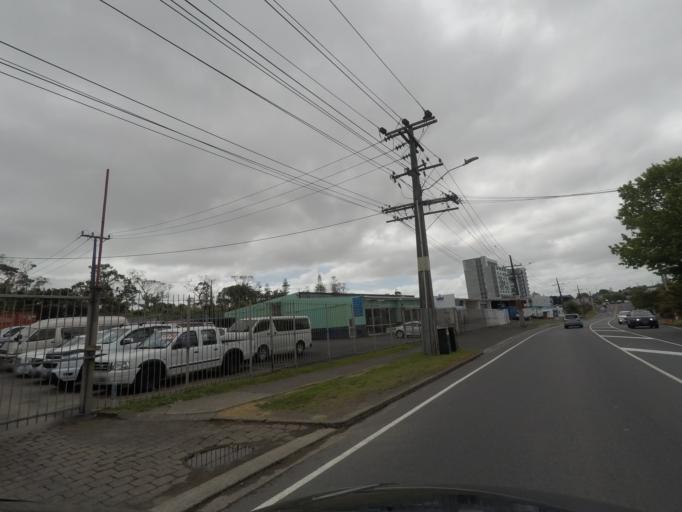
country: NZ
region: Auckland
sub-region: Auckland
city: Waitakere
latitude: -36.9091
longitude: 174.6484
